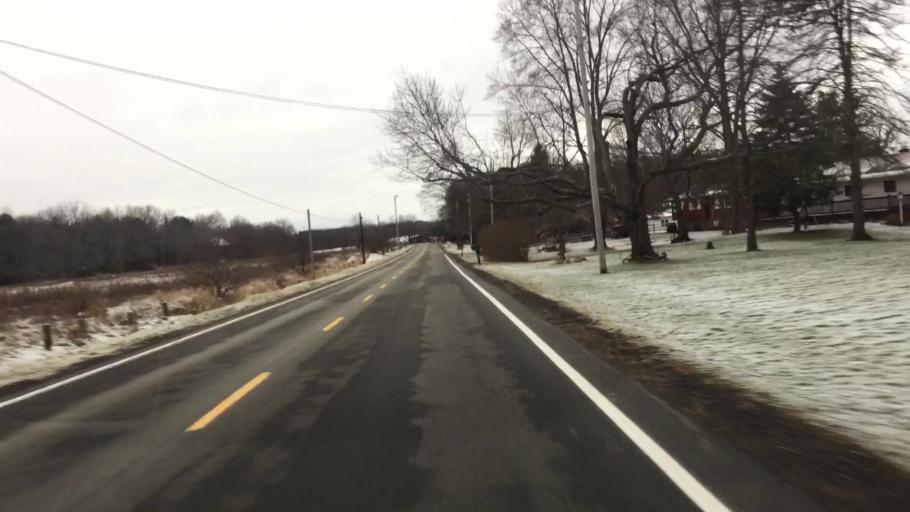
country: US
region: Ohio
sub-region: Summit County
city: Norton
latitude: 41.0725
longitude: -81.6334
